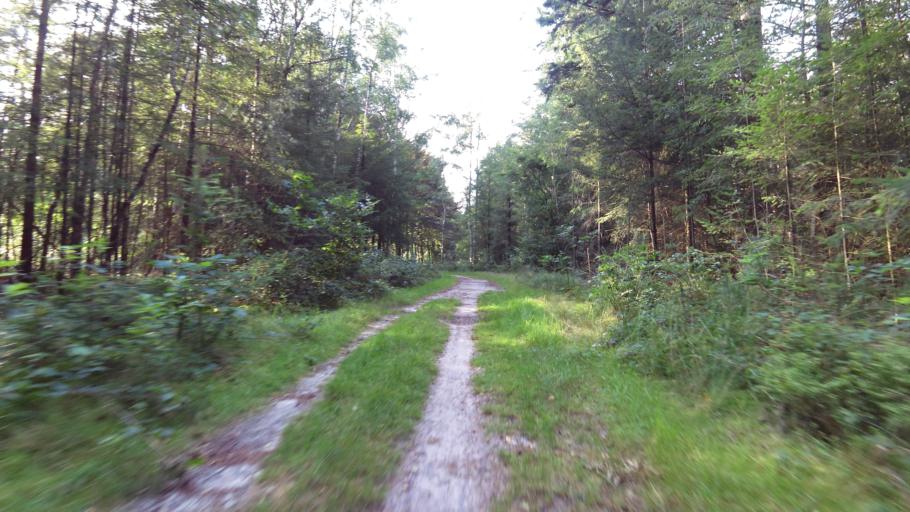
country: NL
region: Utrecht
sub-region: Gemeente Soest
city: Soest
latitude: 52.1560
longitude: 5.2678
